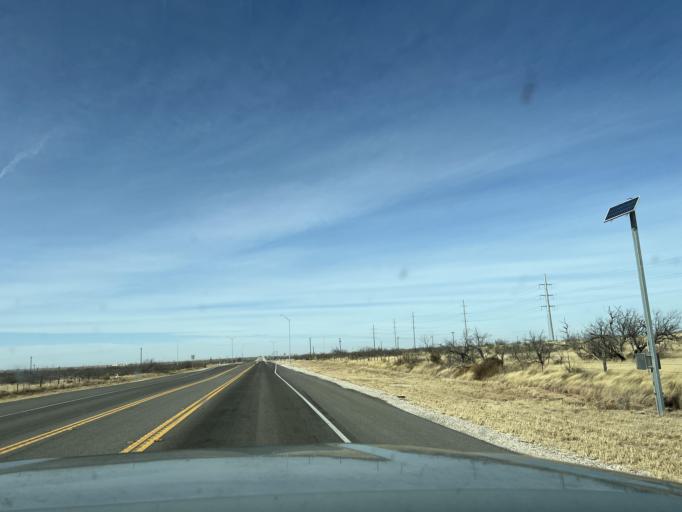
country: US
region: Texas
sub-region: Andrews County
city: Andrews
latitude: 32.3566
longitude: -102.7687
